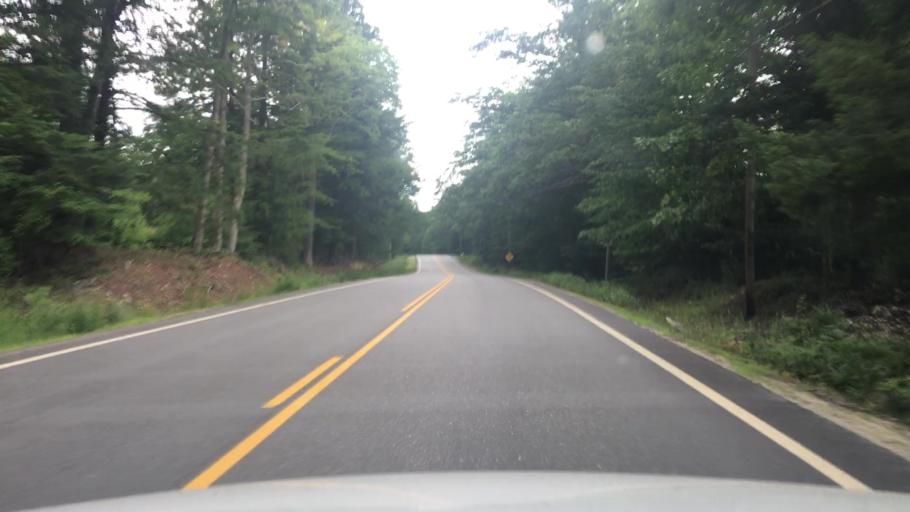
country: US
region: Maine
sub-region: Oxford County
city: Hartford
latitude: 44.3748
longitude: -70.4055
